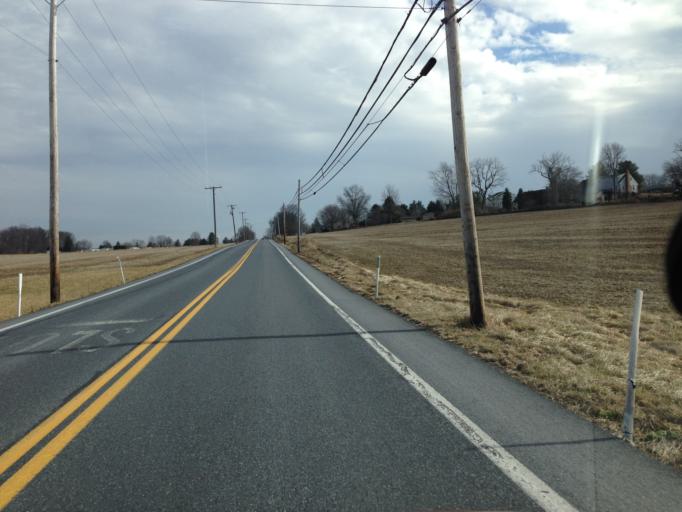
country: US
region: Pennsylvania
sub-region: Lancaster County
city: Penryn
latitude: 40.1797
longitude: -76.3579
